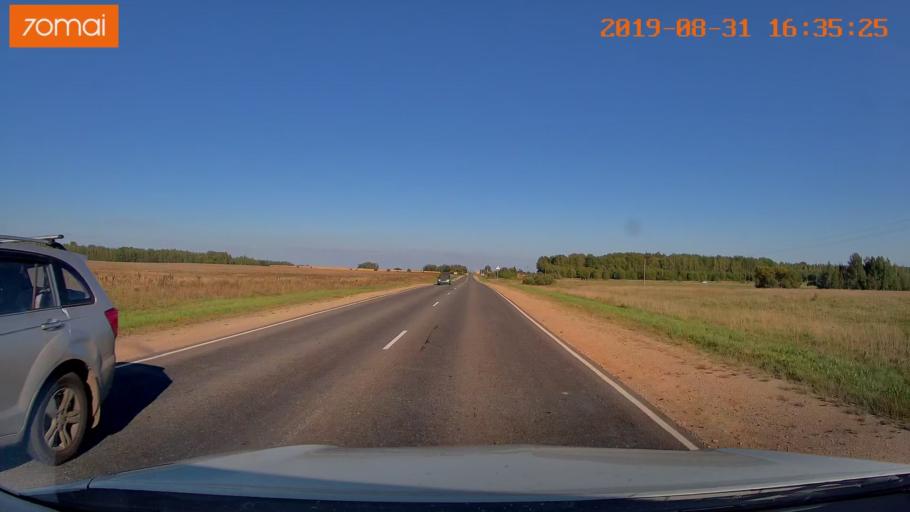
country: RU
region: Kaluga
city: Kurovskoye
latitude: 54.5289
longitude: 35.9454
